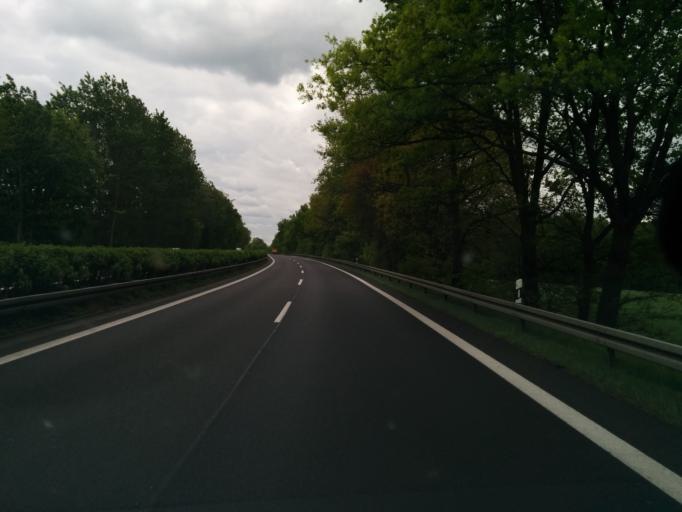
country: DE
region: Brandenburg
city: Werder
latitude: 52.4058
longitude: 12.8761
